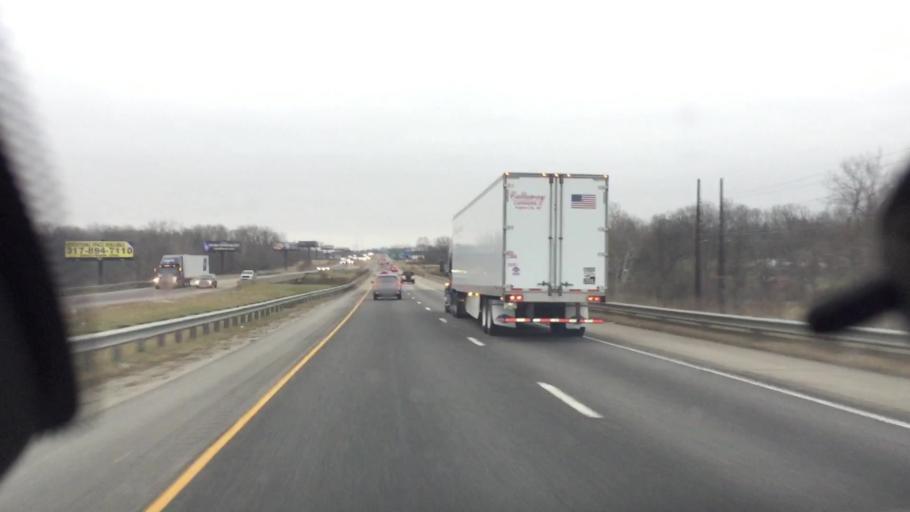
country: US
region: Ohio
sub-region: Preble County
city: New Paris
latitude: 39.8484
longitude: -84.8331
